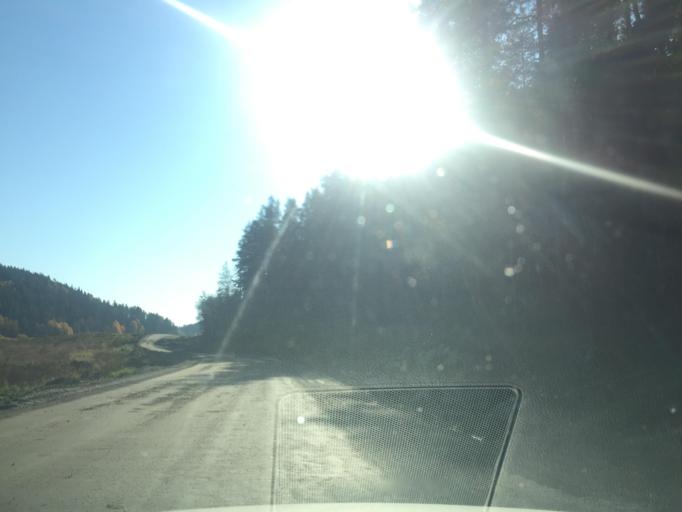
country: RU
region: Leningrad
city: Kuznechnoye
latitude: 61.3238
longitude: 29.8655
